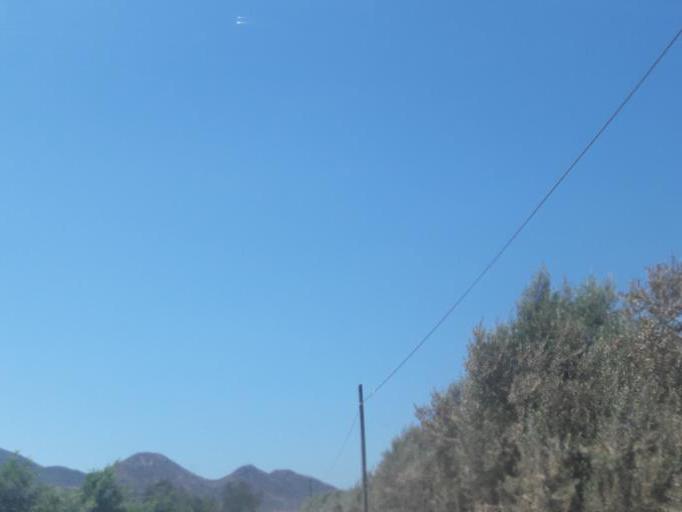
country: MX
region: Baja California
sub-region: Ensenada
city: Rancho Verde
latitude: 32.0852
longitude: -116.6253
